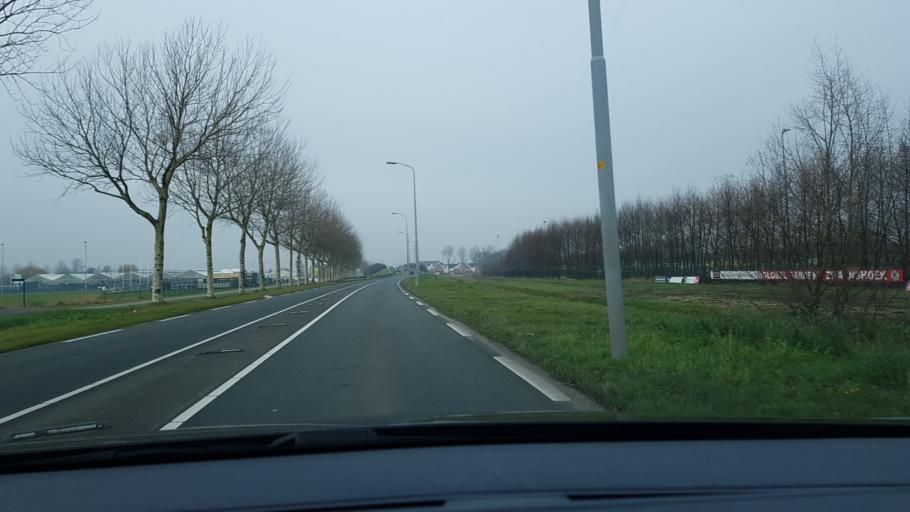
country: NL
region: North Holland
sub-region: Gemeente Haarlemmermeer
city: Hoofddorp
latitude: 52.2927
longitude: 4.6452
